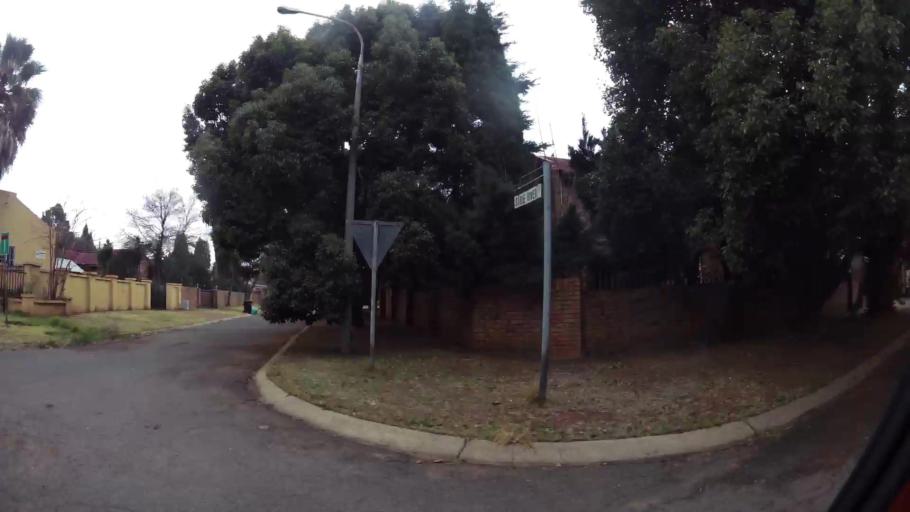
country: ZA
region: Gauteng
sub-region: Sedibeng District Municipality
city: Vanderbijlpark
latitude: -26.7359
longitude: 27.8566
